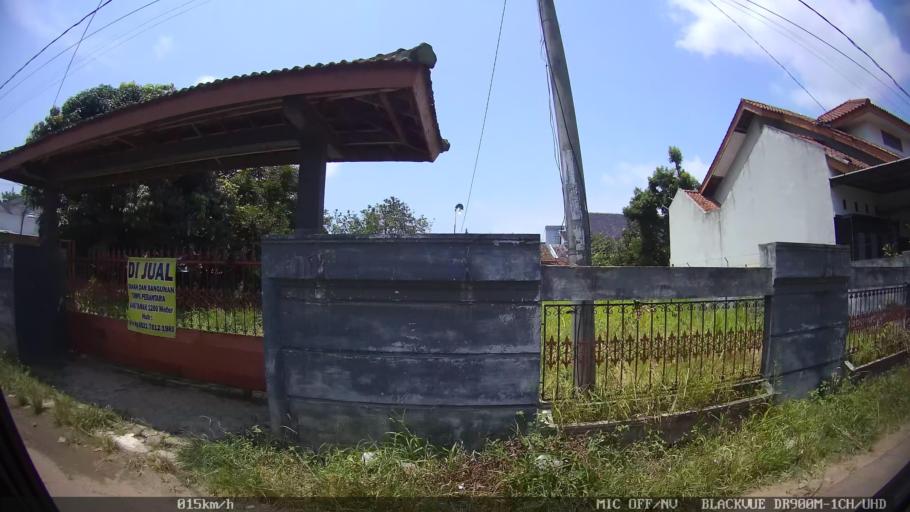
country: ID
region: Lampung
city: Kedaton
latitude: -5.3719
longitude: 105.2708
